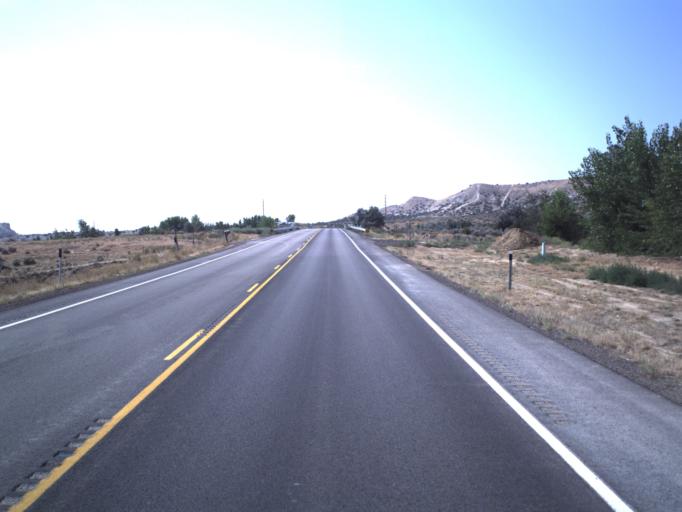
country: US
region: Utah
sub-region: Uintah County
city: Naples
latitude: 40.3653
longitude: -109.4983
